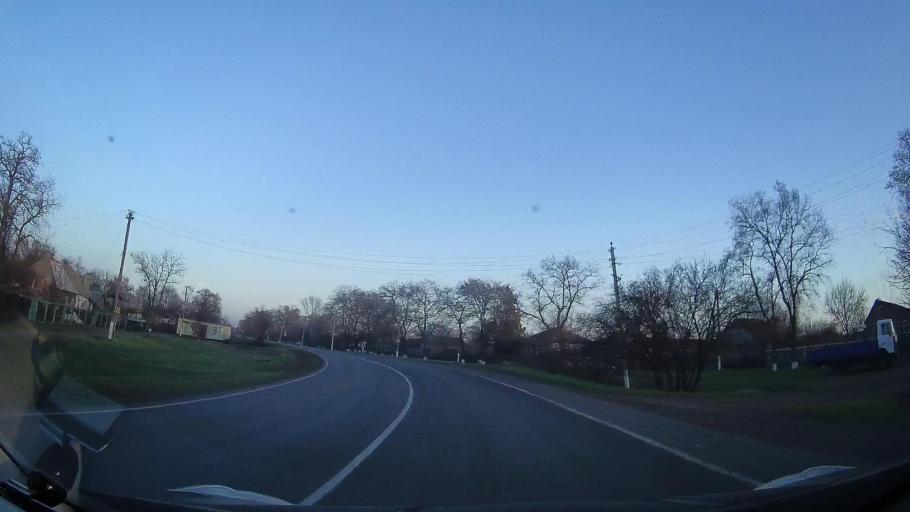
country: RU
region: Rostov
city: Bagayevskaya
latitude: 47.0930
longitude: 40.3159
